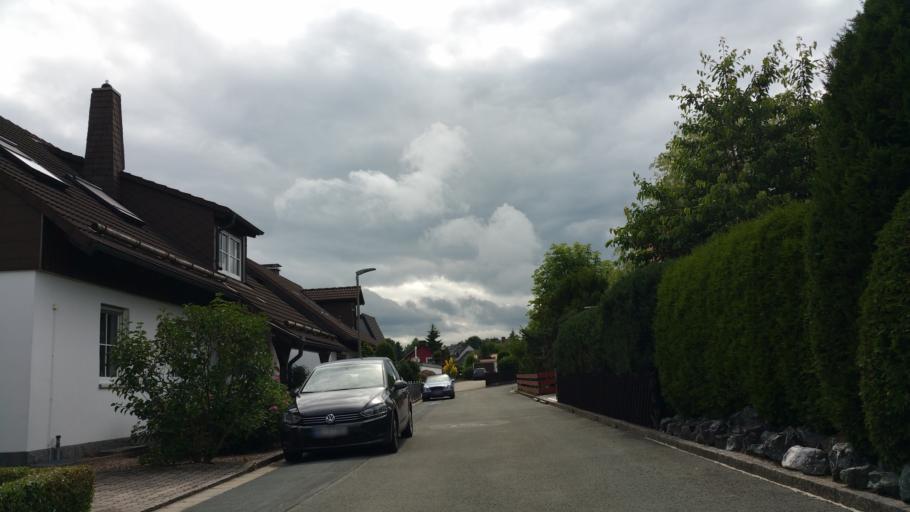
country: DE
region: Bavaria
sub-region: Upper Franconia
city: Rehau
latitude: 50.2553
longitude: 12.0355
